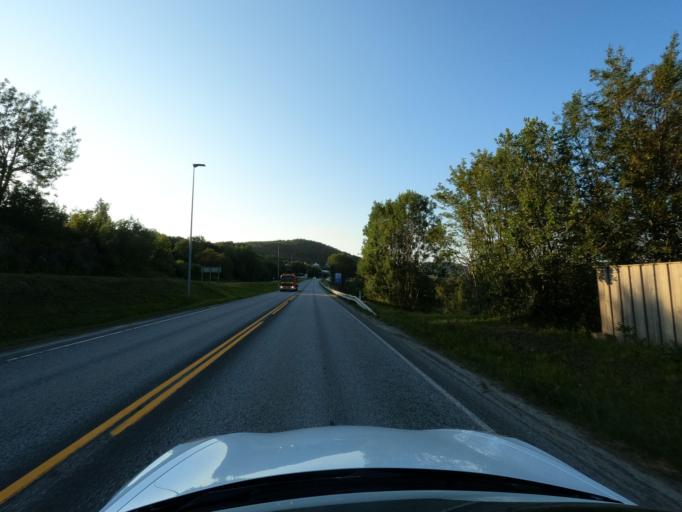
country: NO
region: Troms
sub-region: Harstad
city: Harstad
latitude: 68.7681
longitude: 16.5588
